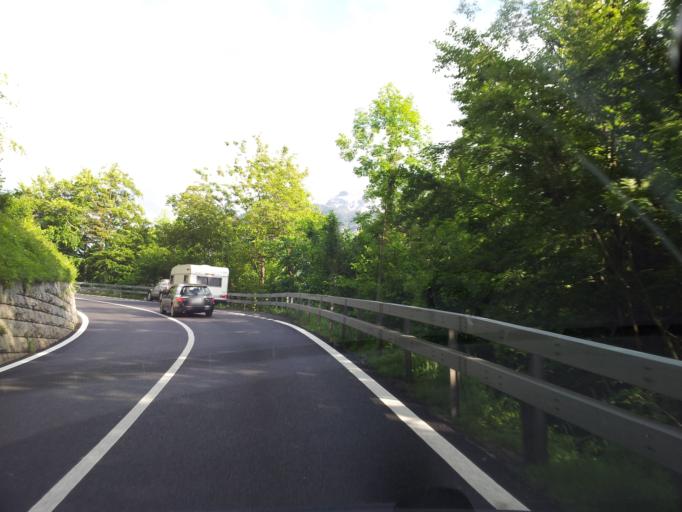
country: CH
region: Obwalden
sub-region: Obwalden
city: Lungern
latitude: 46.7503
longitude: 8.1111
